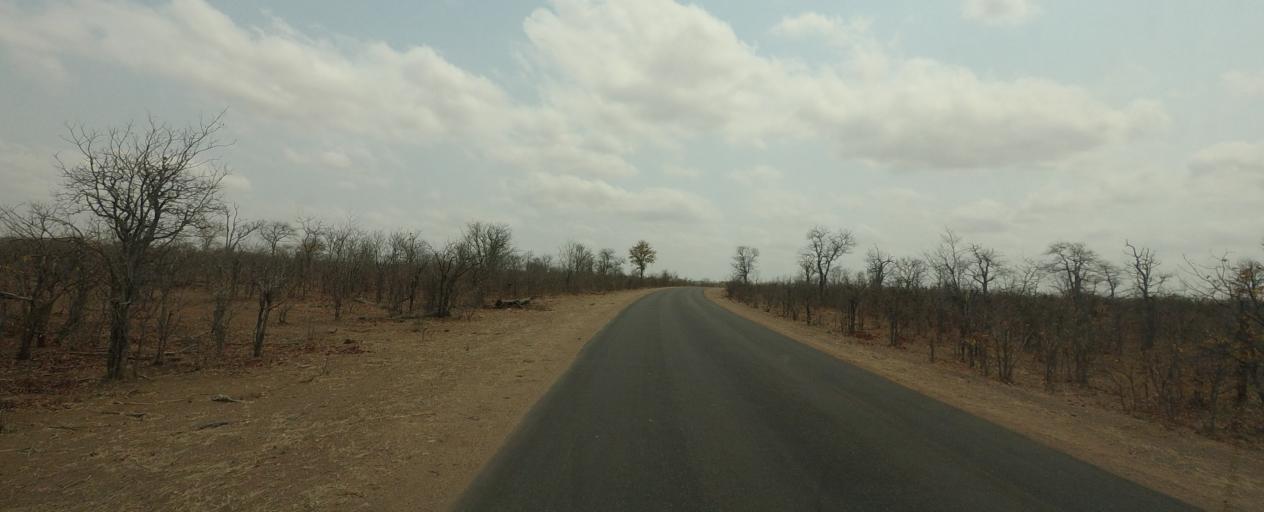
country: ZA
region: Limpopo
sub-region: Mopani District Municipality
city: Phalaborwa
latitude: -23.5501
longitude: 31.4303
